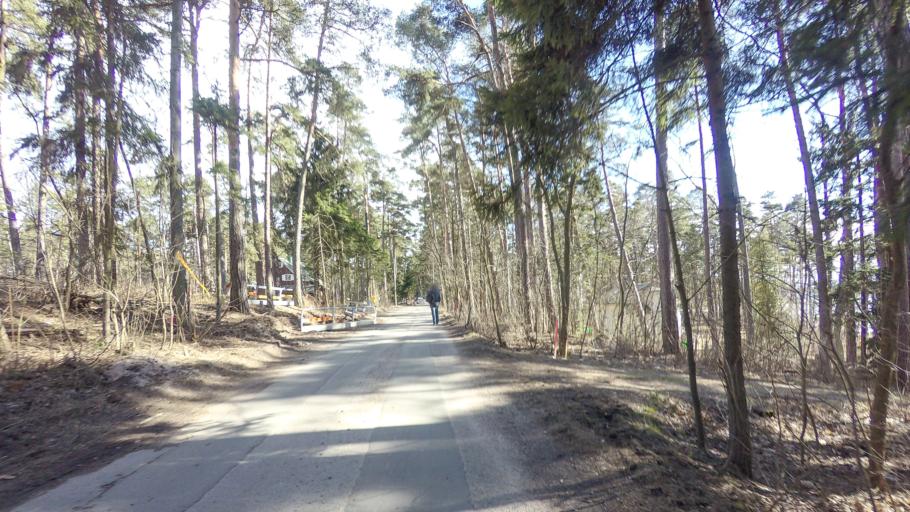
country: FI
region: Uusimaa
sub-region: Helsinki
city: Vantaa
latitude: 60.1933
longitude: 25.1352
